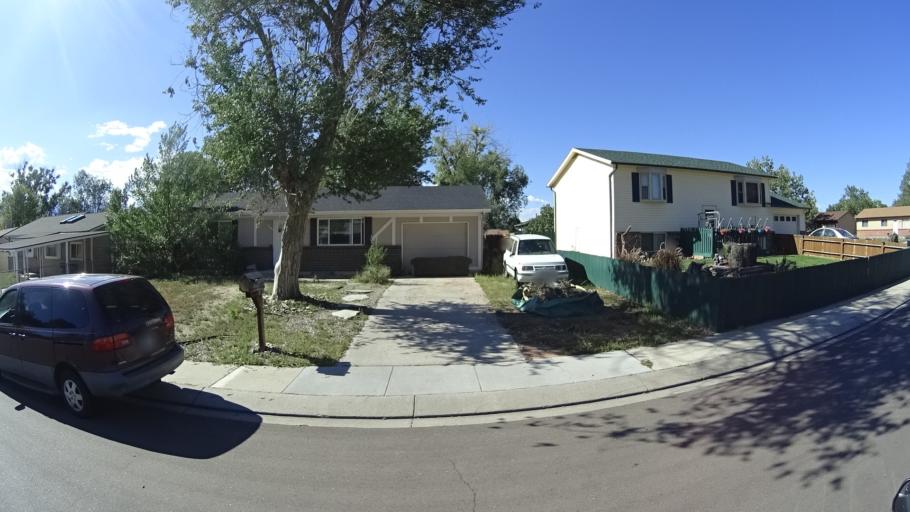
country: US
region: Colorado
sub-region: El Paso County
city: Stratmoor
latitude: 38.7993
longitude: -104.7463
